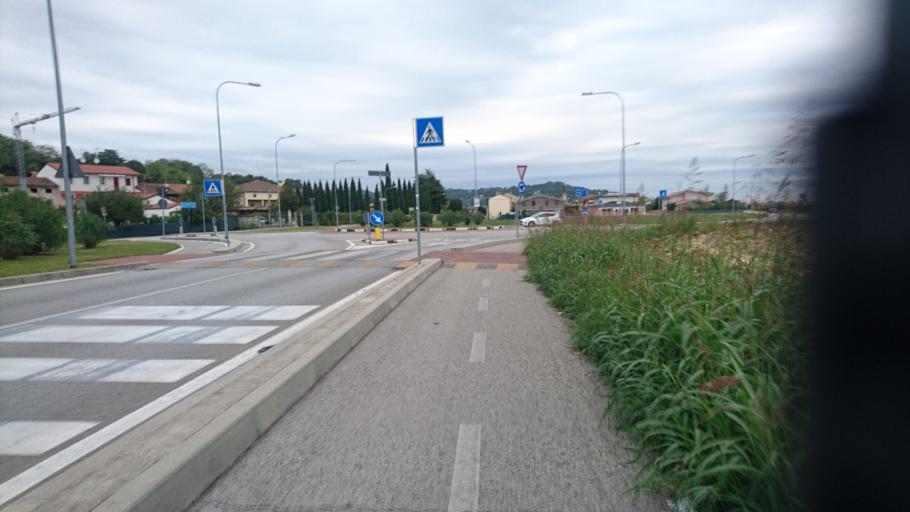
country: IT
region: Veneto
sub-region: Provincia di Vicenza
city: Sovizzo
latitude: 45.5191
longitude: 11.4332
